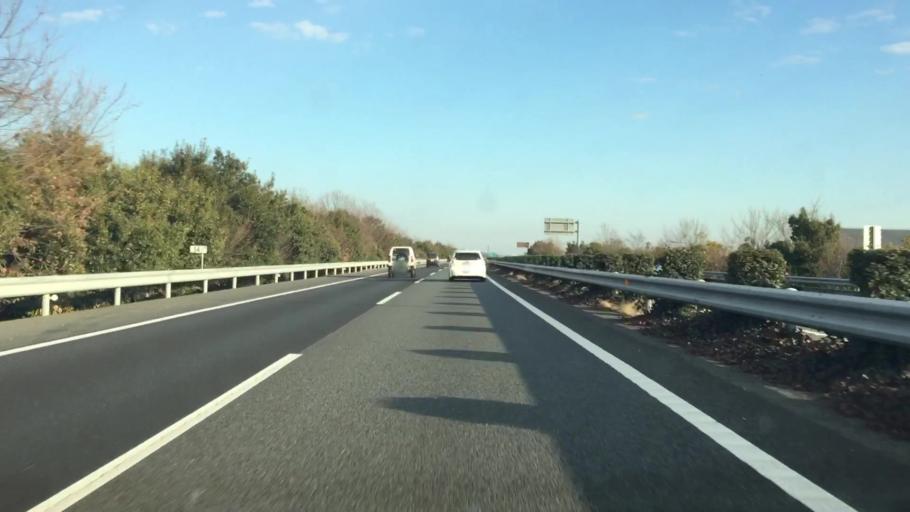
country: JP
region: Gunma
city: Isesaki
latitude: 36.3542
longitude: 139.2226
